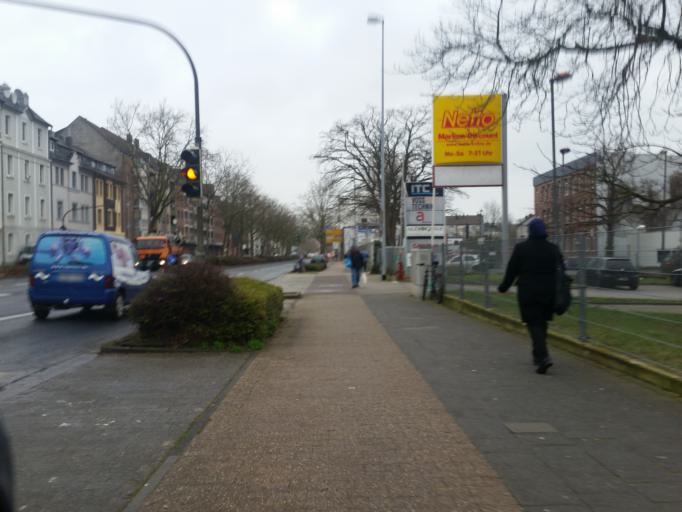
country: DE
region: North Rhine-Westphalia
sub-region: Regierungsbezirk Koln
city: Aachen
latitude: 50.7885
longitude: 6.1150
